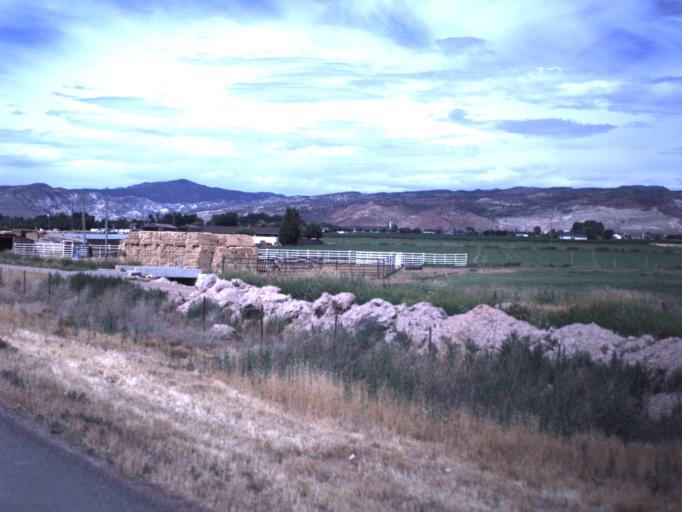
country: US
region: Utah
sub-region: Sevier County
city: Richfield
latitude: 38.7818
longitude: -112.0597
